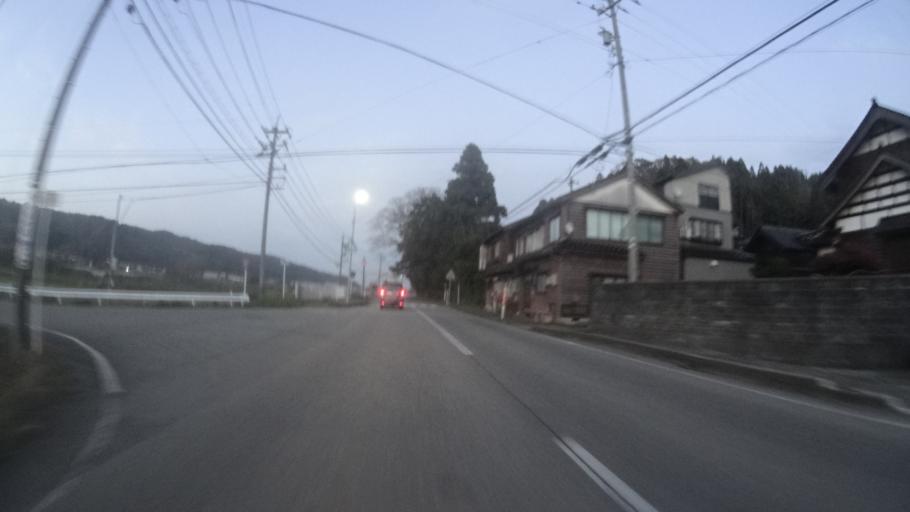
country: JP
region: Ishikawa
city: Nanao
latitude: 37.3714
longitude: 136.8764
